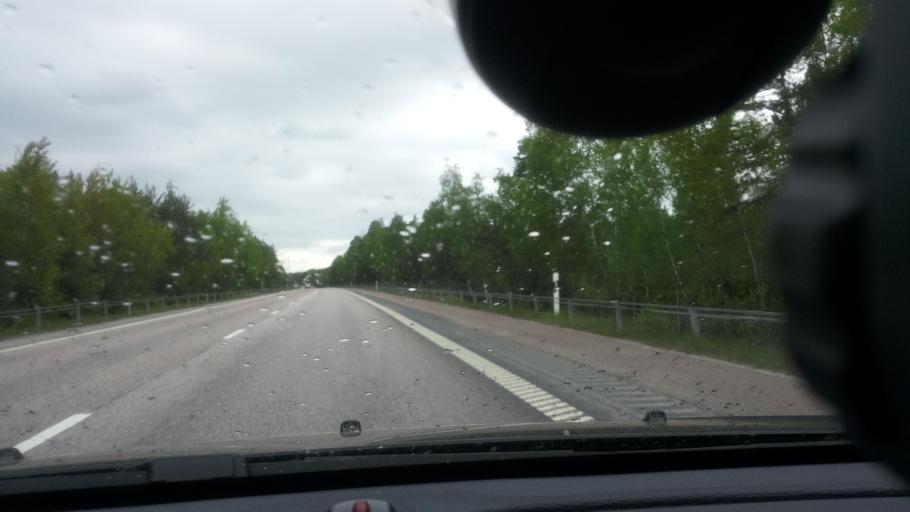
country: SE
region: Stockholm
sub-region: Sigtuna Kommun
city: Marsta
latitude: 59.6528
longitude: 17.8893
